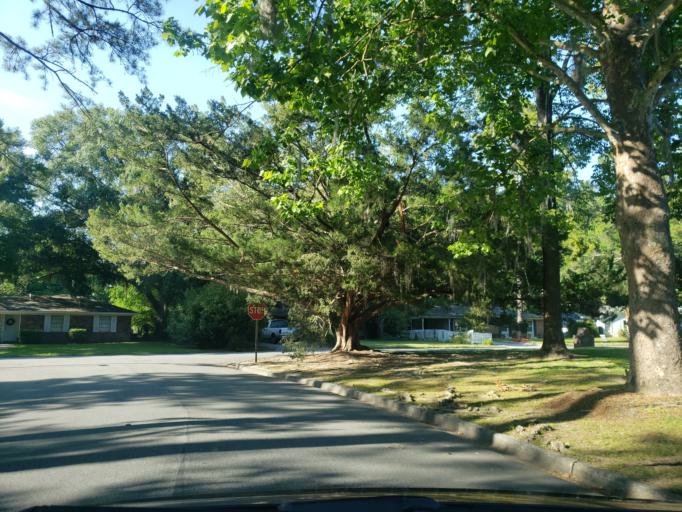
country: US
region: Georgia
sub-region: Chatham County
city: Montgomery
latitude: 31.9867
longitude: -81.1488
